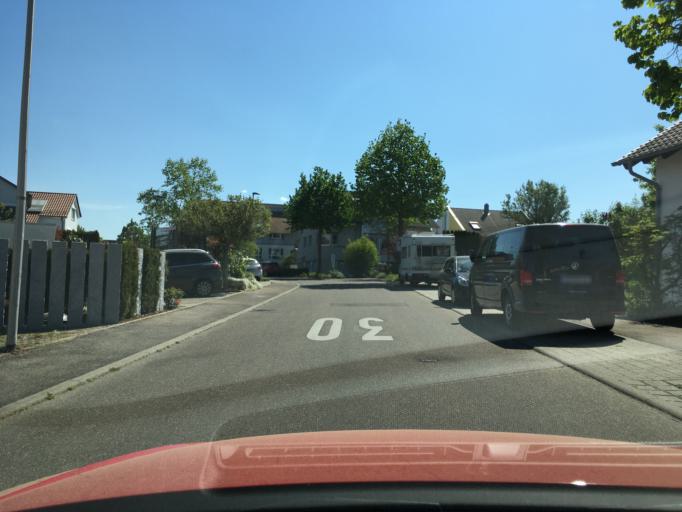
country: DE
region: Baden-Wuerttemberg
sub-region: Regierungsbezirk Stuttgart
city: Flein
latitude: 49.1004
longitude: 9.2024
